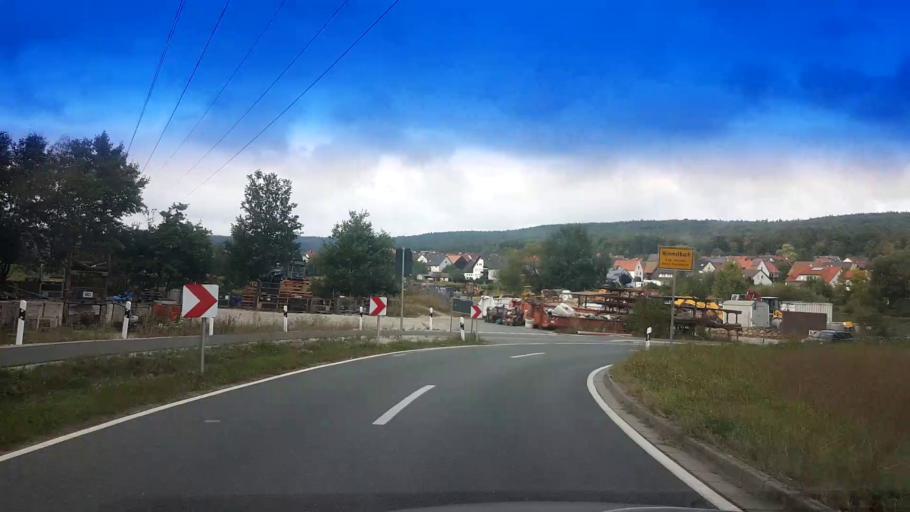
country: DE
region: Bavaria
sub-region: Upper Franconia
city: Heroldsbach
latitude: 49.7025
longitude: 11.0107
